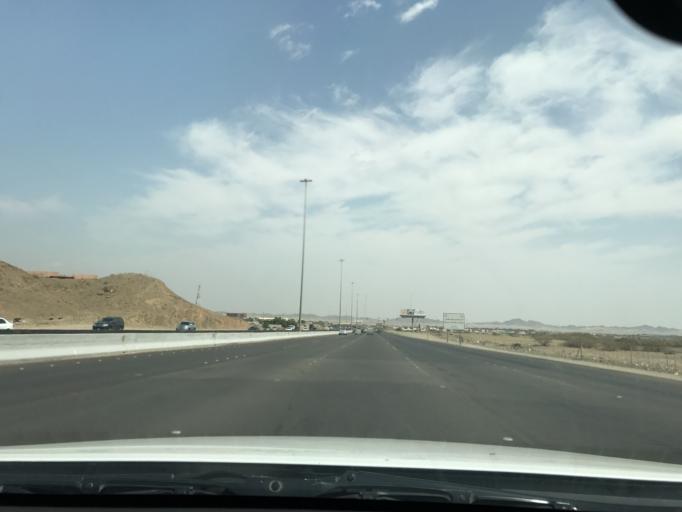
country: SA
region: Makkah
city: Jeddah
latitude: 21.3979
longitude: 39.4079
